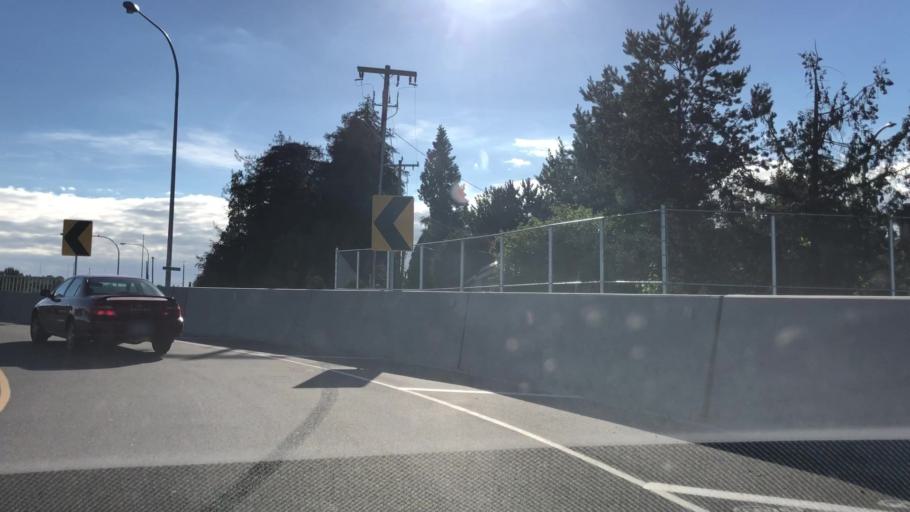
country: US
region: Washington
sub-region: King County
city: Seattle
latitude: 47.6452
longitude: -122.3016
